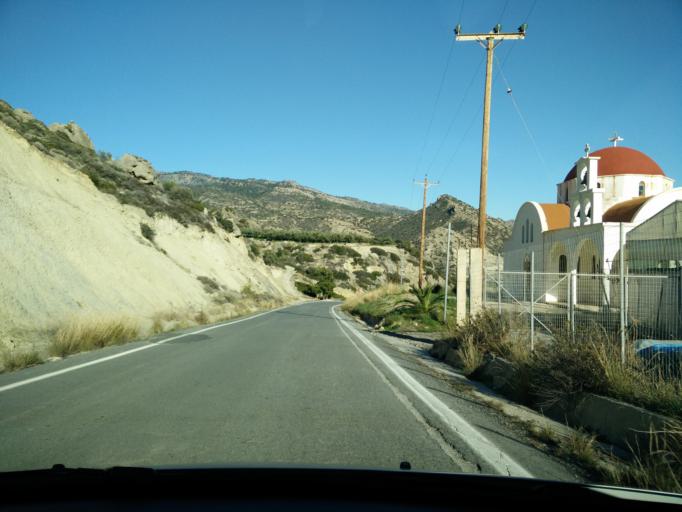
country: GR
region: Crete
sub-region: Nomos Lasithiou
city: Gra Liyia
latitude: 35.0157
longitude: 25.5793
